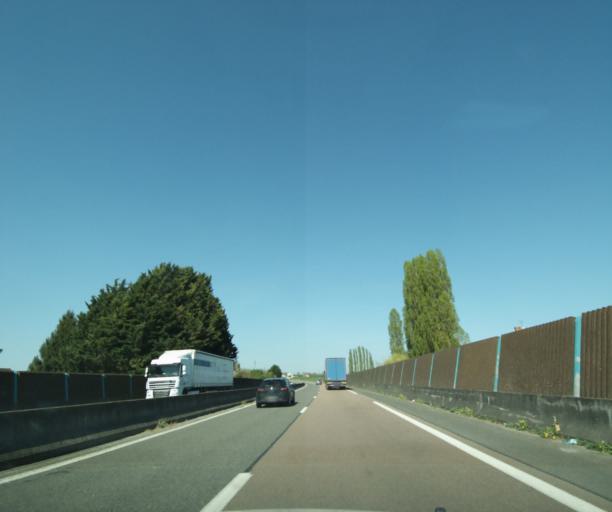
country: FR
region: Bourgogne
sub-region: Departement de la Nievre
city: Cosne-Cours-sur-Loire
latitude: 47.4076
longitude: 2.9445
